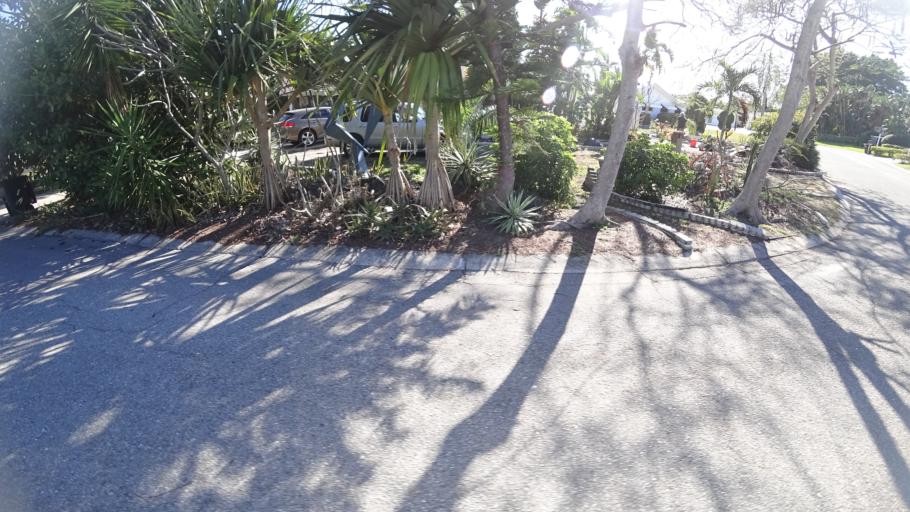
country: US
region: Florida
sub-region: Manatee County
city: Bayshore Gardens
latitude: 27.4236
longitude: -82.5960
